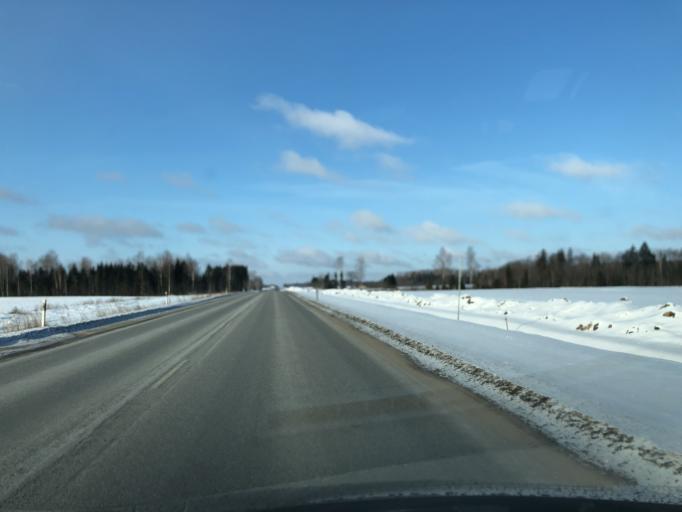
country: EE
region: Jogevamaa
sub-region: Tabivere vald
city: Tabivere
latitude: 58.4368
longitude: 26.4650
